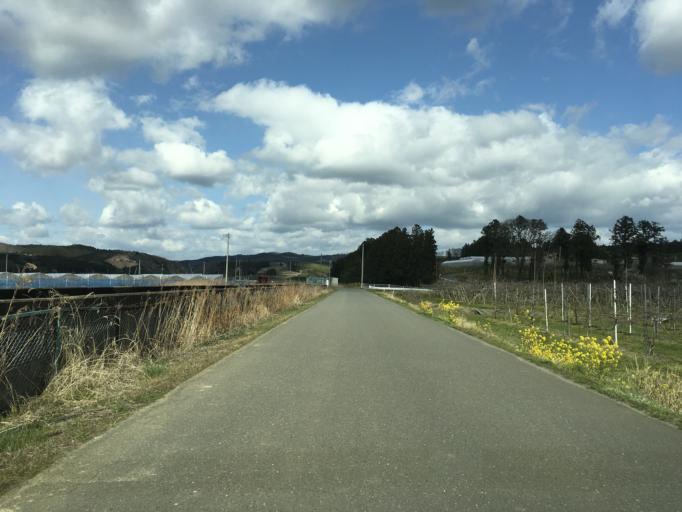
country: JP
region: Iwate
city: Ichinoseki
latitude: 38.7506
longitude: 141.2615
